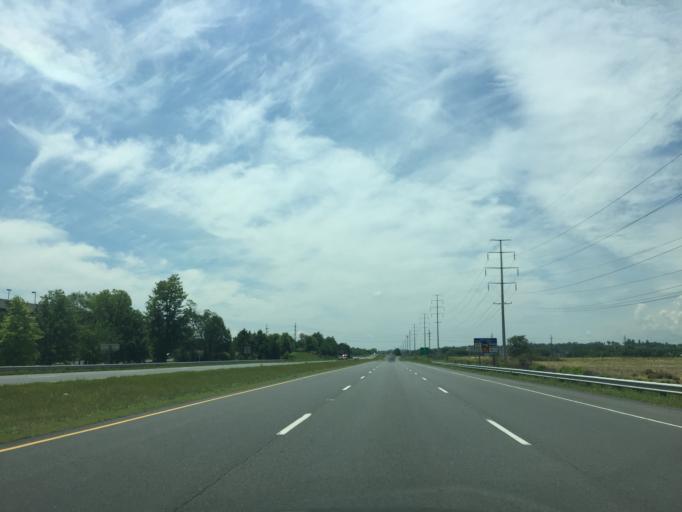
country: US
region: Virginia
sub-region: City of Winchester
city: Winchester
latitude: 39.1987
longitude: -78.1932
